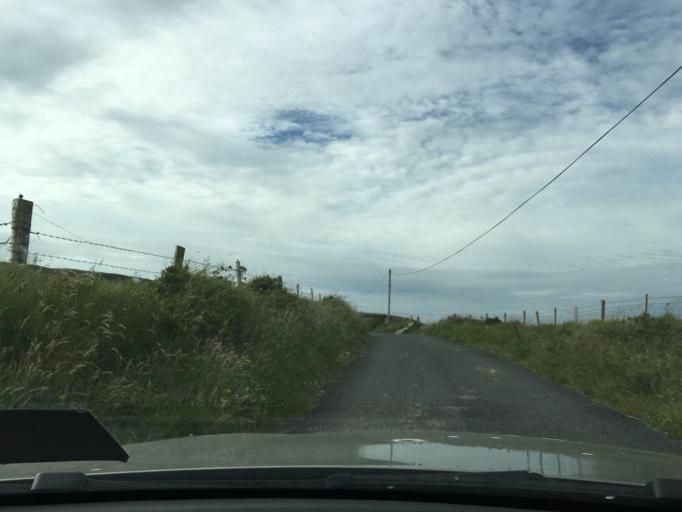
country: IE
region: Ulster
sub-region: County Donegal
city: Carndonagh
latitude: 55.3282
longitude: -7.3127
